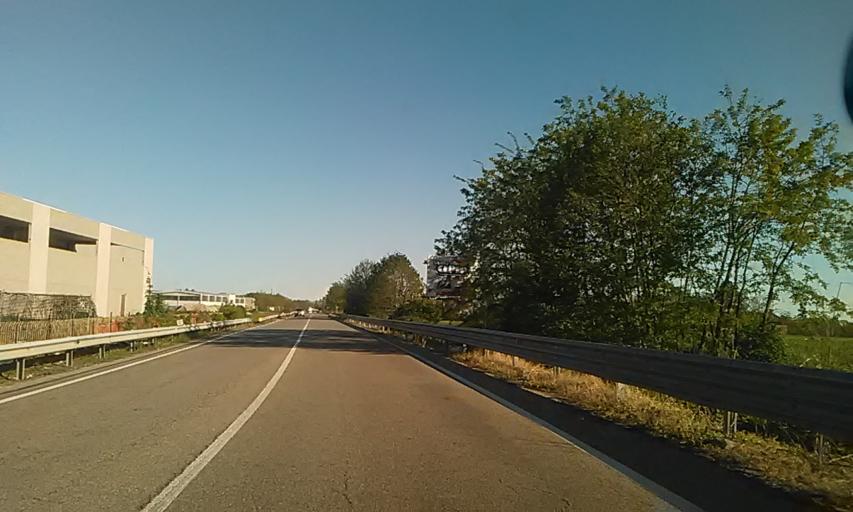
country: IT
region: Piedmont
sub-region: Provincia di Novara
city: Vaprio D'Agogna
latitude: 45.5939
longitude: 8.5387
